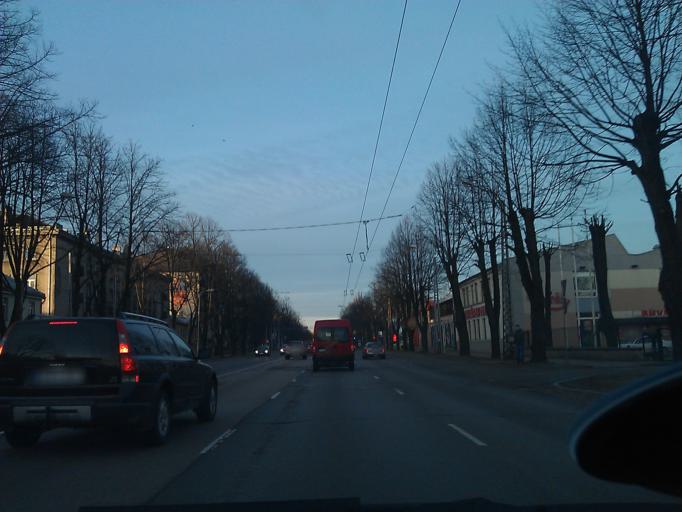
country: LV
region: Riga
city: Jaunciems
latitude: 56.9820
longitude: 24.1949
